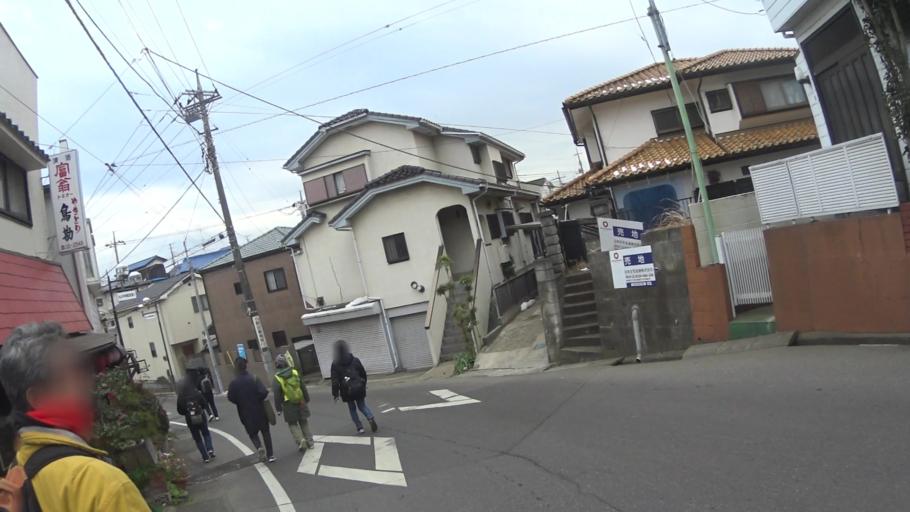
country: JP
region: Chiba
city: Funabashi
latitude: 35.7487
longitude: 139.9917
